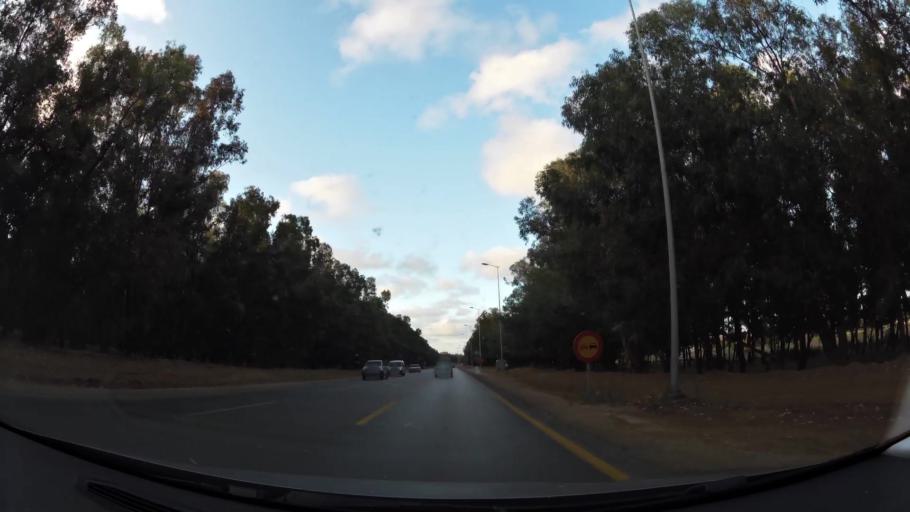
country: MA
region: Gharb-Chrarda-Beni Hssen
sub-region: Kenitra Province
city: Kenitra
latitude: 34.2418
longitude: -6.6249
